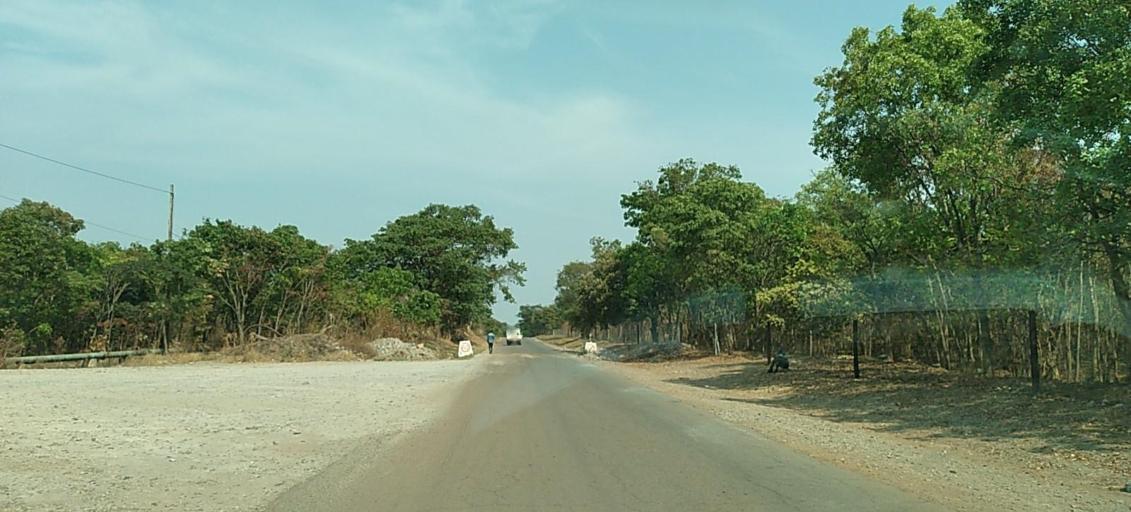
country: ZM
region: Copperbelt
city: Chililabombwe
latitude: -12.3077
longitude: 27.7912
